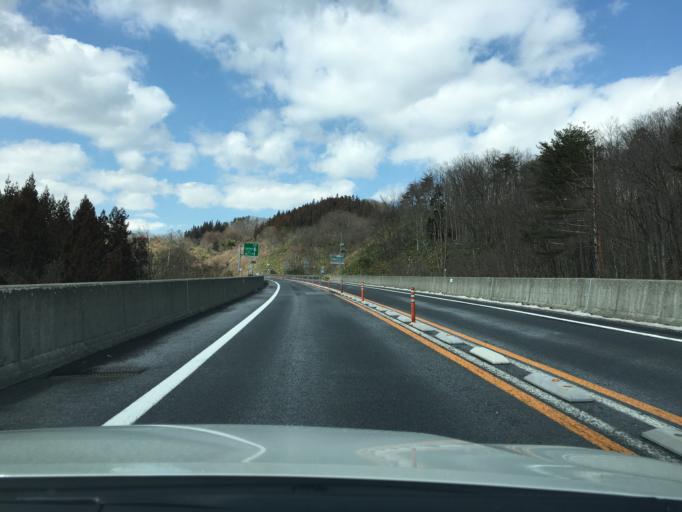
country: JP
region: Yamagata
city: Sagae
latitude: 38.4159
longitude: 140.1889
